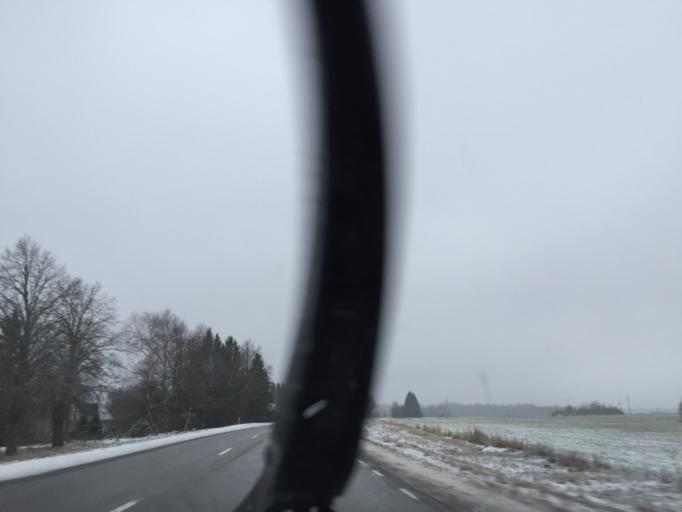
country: EE
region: Laeaene
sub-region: Lihula vald
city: Lihula
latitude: 58.5613
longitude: 23.9874
